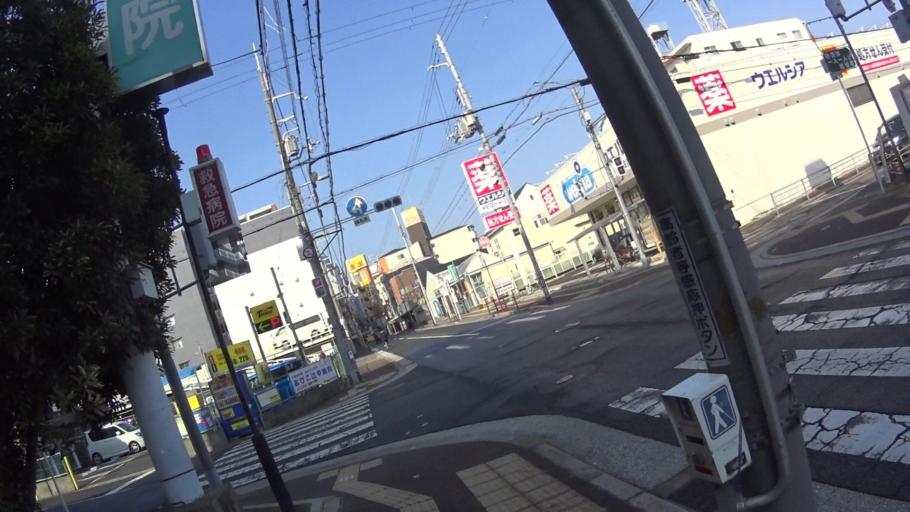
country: JP
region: Osaka
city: Sakai
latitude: 34.6008
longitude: 135.5098
